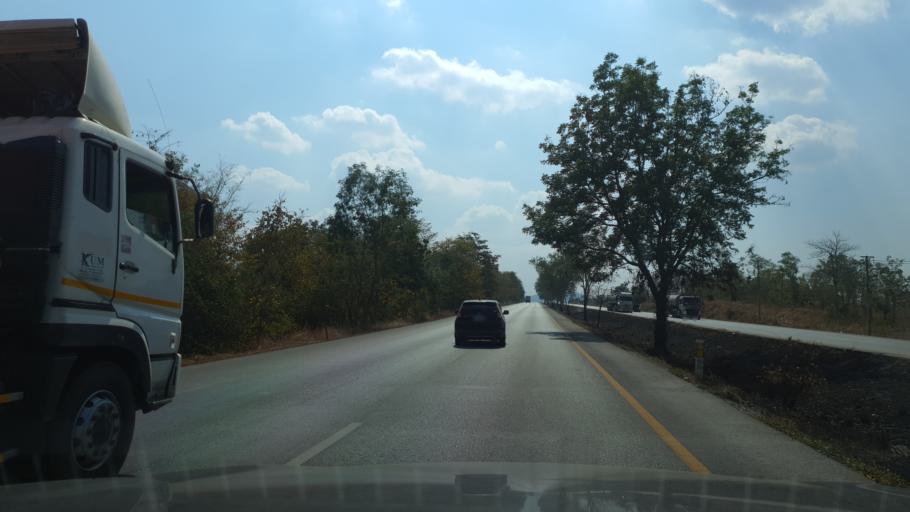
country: TH
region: Lampang
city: Mae Phrik
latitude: 17.3921
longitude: 99.1489
